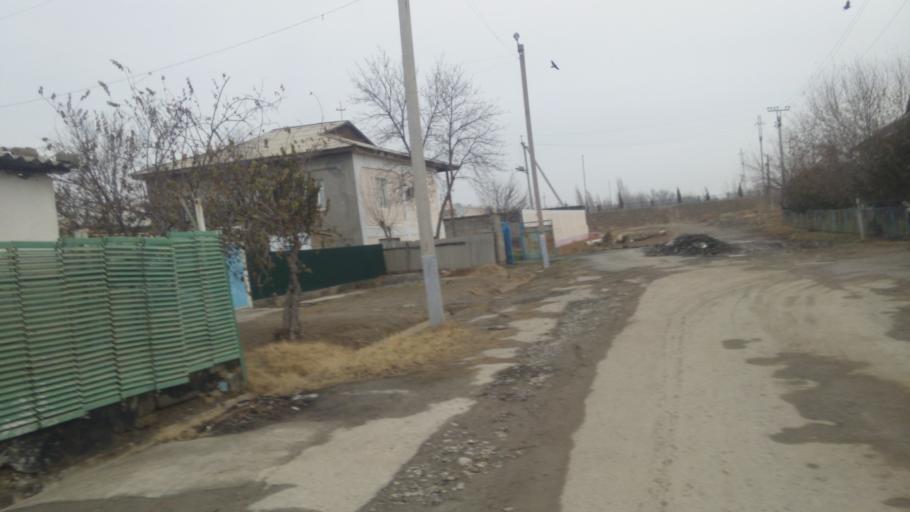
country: UZ
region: Sirdaryo
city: Guliston
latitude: 40.5044
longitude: 68.7800
